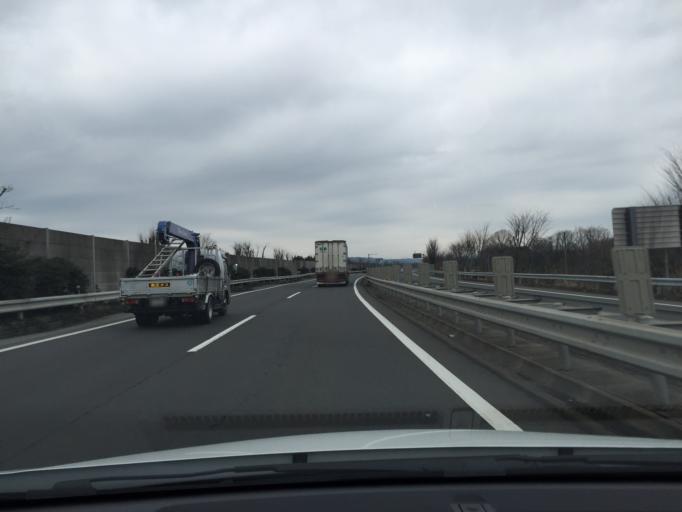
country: JP
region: Saitama
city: Sayama
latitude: 35.8612
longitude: 139.3767
